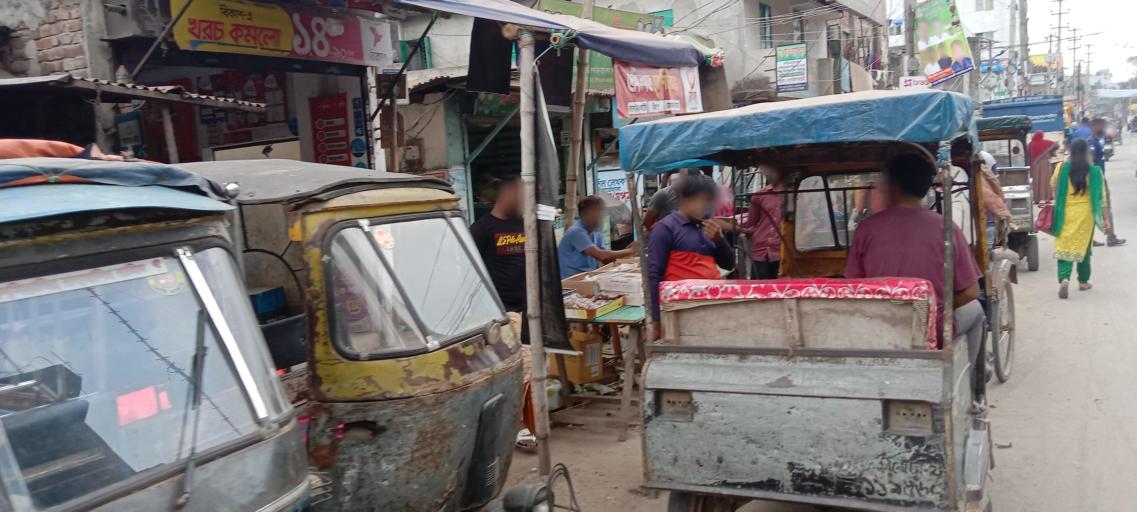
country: BD
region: Dhaka
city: Azimpur
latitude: 23.7299
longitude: 90.3354
